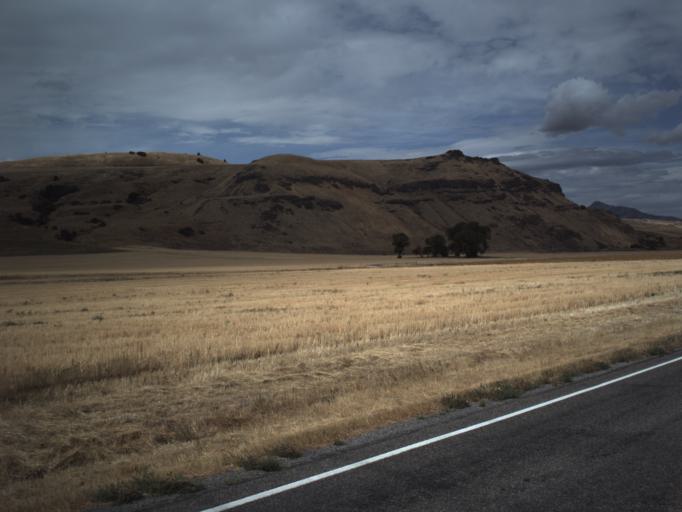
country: US
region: Utah
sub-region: Cache County
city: Benson
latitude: 41.7845
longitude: -111.9867
